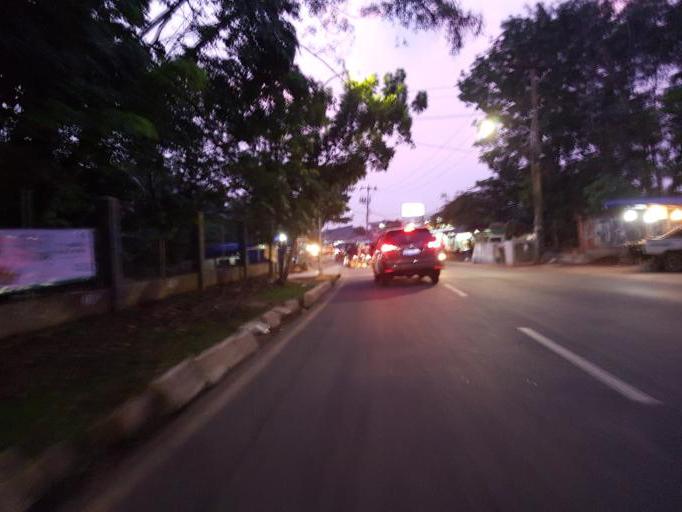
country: ID
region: West Java
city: Serpong
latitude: -6.3268
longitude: 106.6716
